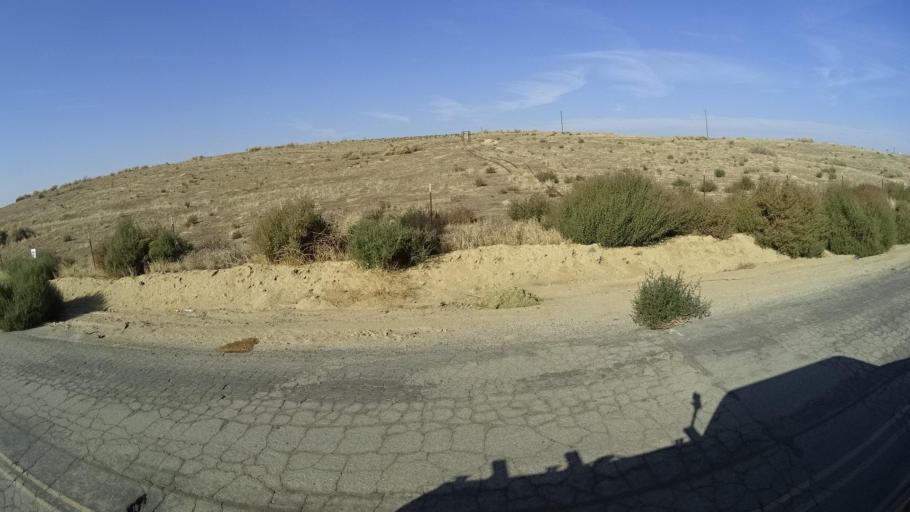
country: US
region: California
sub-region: Kern County
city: Oildale
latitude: 35.4903
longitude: -119.0430
